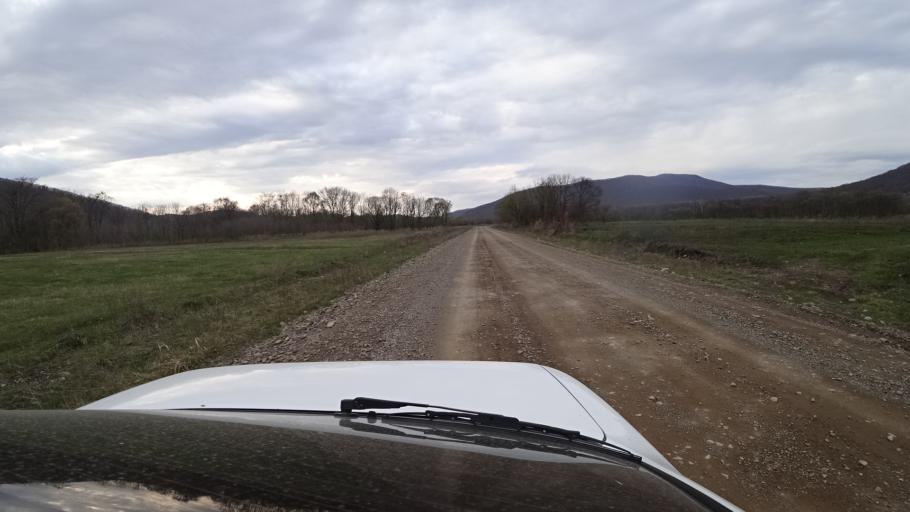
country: RU
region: Primorskiy
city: Novopokrovka
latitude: 45.1495
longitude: 134.3816
